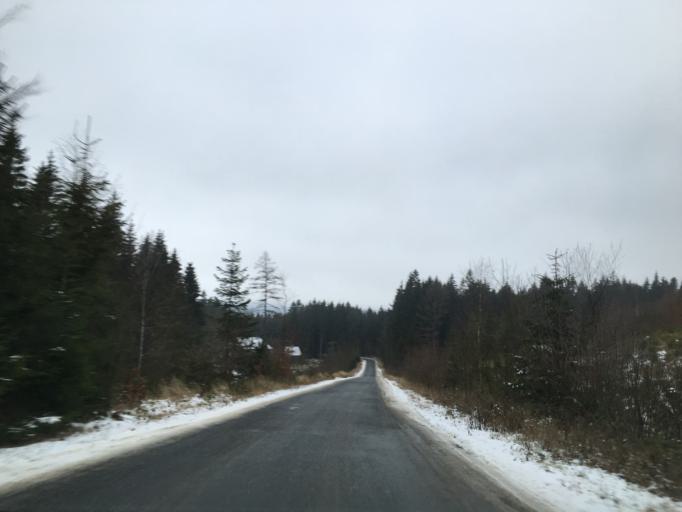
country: PL
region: Lower Silesian Voivodeship
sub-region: Powiat kamiennogorski
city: Krzeszow
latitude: 50.6564
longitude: 16.0949
